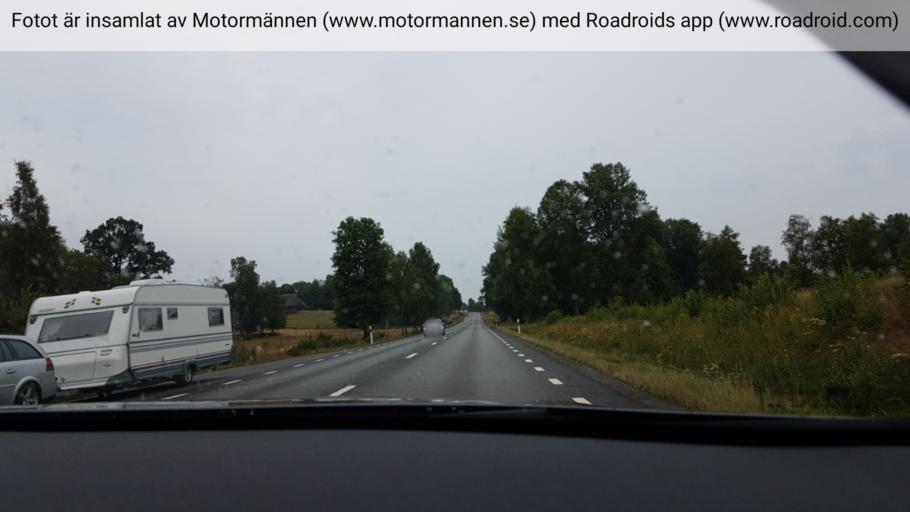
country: SE
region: Joenkoeping
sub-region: Varnamo Kommun
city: Varnamo
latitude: 57.2125
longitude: 14.1044
